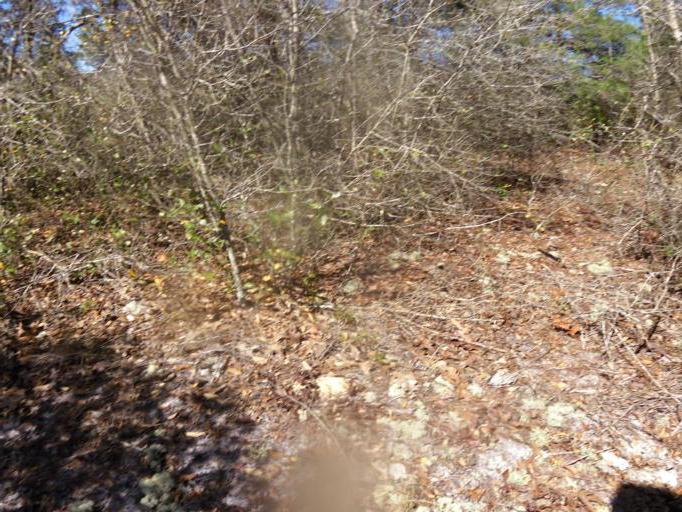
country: US
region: Florida
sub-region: Clay County
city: Keystone Heights
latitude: 29.8385
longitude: -81.9840
